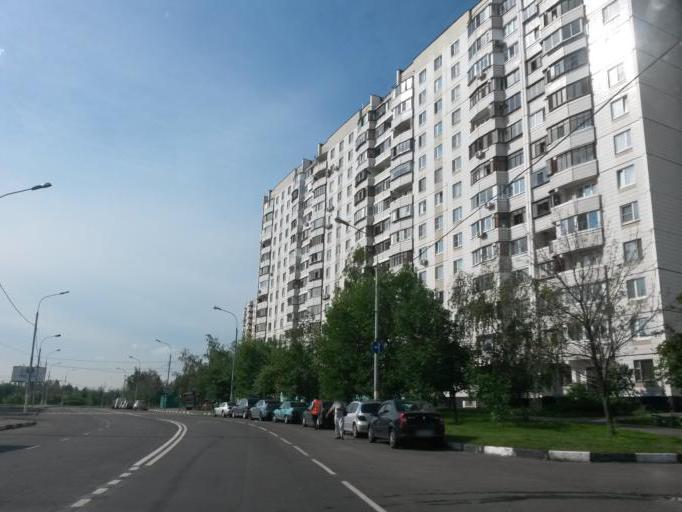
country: RU
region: Moscow
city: Brateyevo
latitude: 55.6346
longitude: 37.7698
